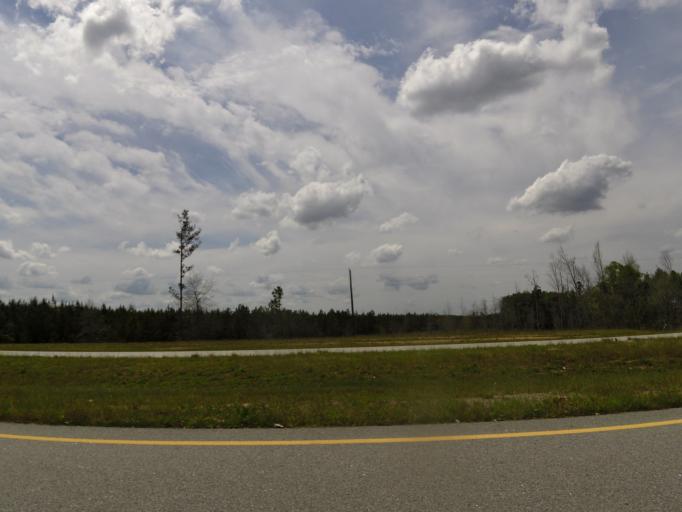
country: US
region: Georgia
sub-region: Jefferson County
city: Wadley
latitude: 32.7355
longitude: -82.3946
